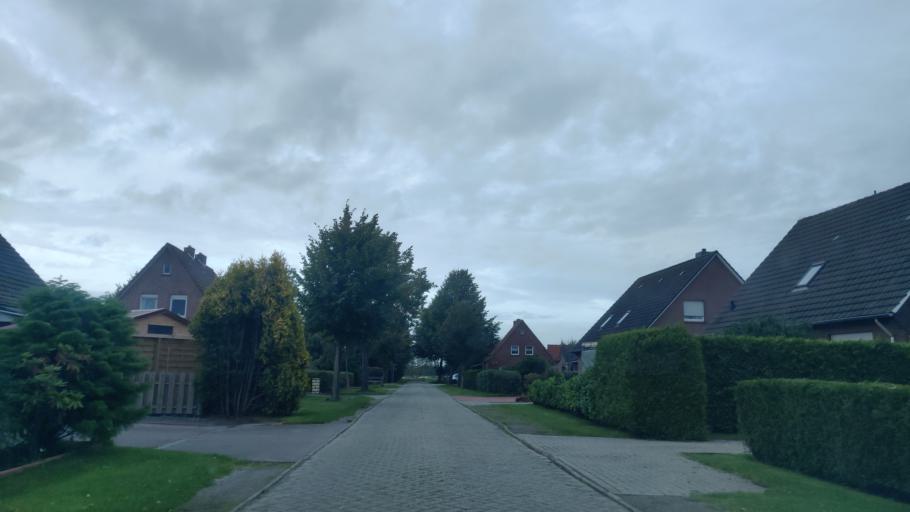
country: DE
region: Lower Saxony
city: Rechtsupweg
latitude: 53.4834
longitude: 7.3990
